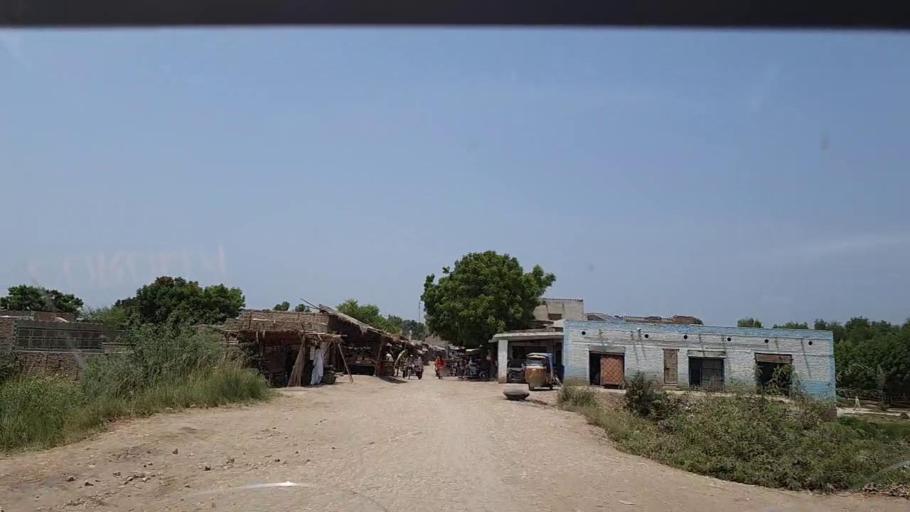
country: PK
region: Sindh
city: Pano Aqil
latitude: 27.9206
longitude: 69.1961
